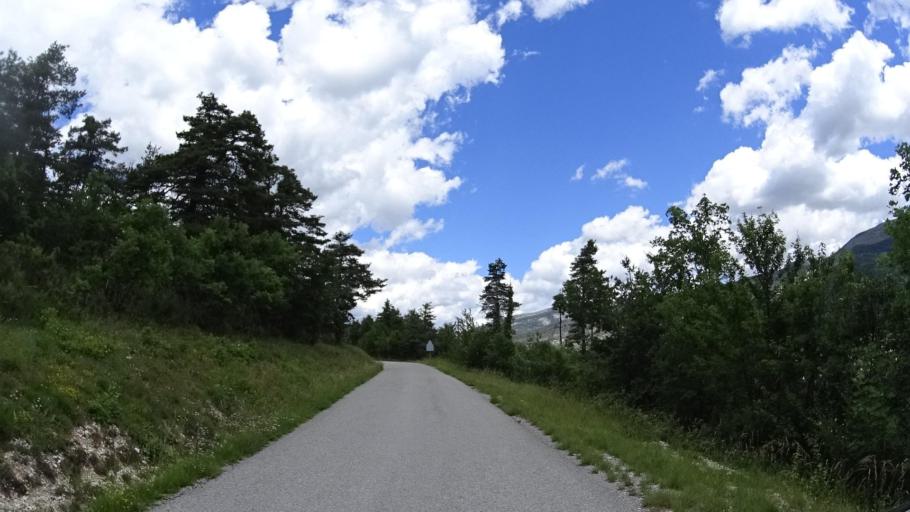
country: FR
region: Provence-Alpes-Cote d'Azur
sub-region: Departement des Alpes-de-Haute-Provence
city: Annot
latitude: 44.0131
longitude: 6.6285
